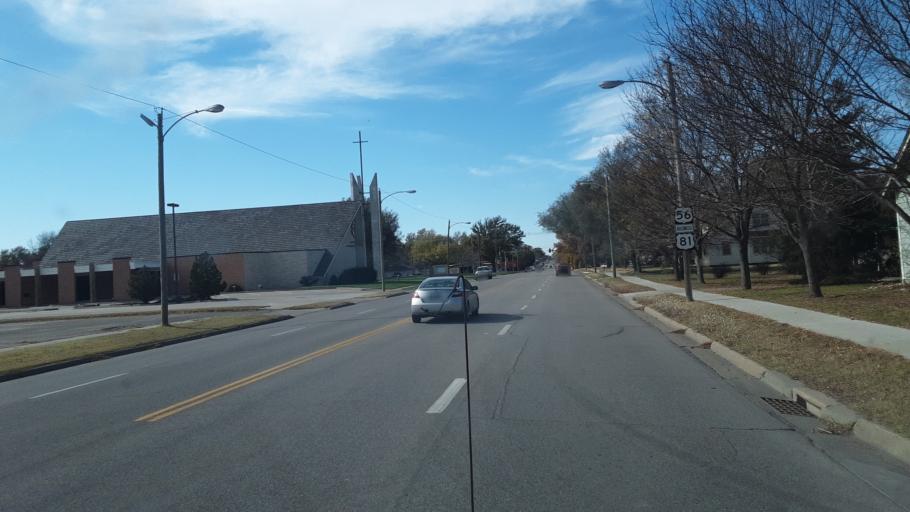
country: US
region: Kansas
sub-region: McPherson County
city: McPherson
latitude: 38.3695
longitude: -97.6459
